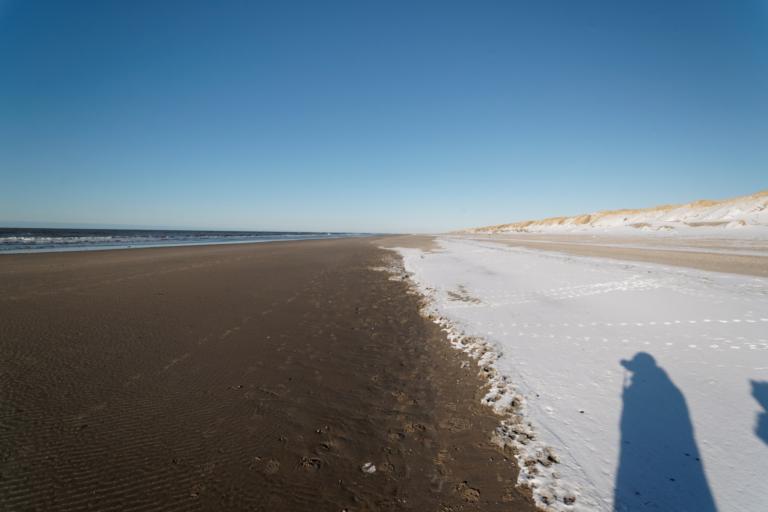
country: NL
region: North Holland
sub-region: Gemeente Texel
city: Den Burg
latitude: 53.1465
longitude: 4.8030
